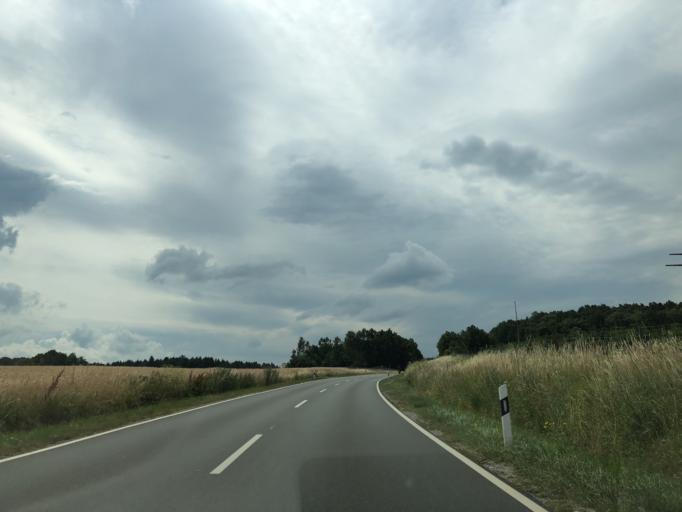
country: DE
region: Bavaria
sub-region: Regierungsbezirk Mittelfranken
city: Muhlhausen
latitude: 49.7409
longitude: 10.7881
